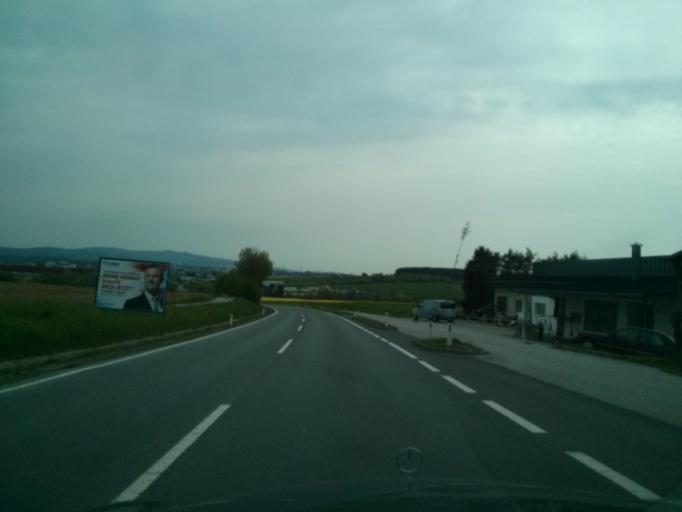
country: AT
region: Burgenland
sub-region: Politischer Bezirk Oberwart
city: Oberwart
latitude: 47.2803
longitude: 16.1755
